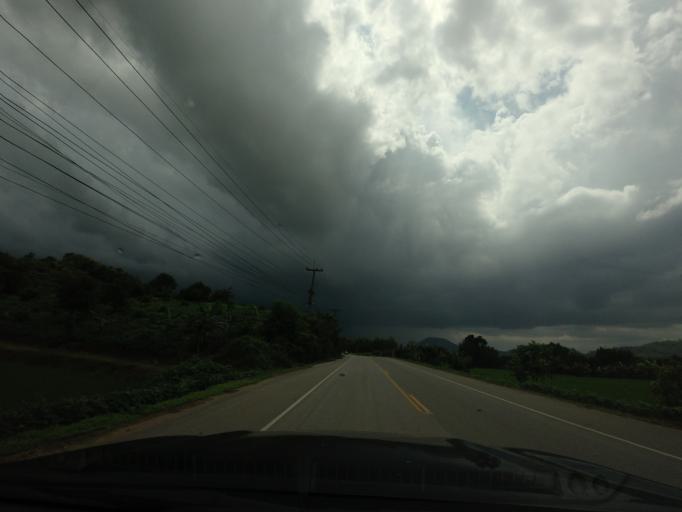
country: LA
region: Vientiane
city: Muang Sanakham
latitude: 17.9815
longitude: 101.7478
